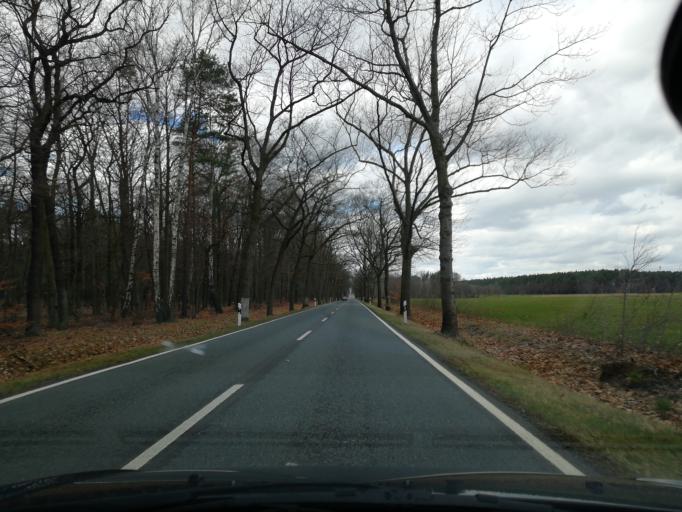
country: DE
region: Brandenburg
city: Altdobern
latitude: 51.7016
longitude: 14.0721
